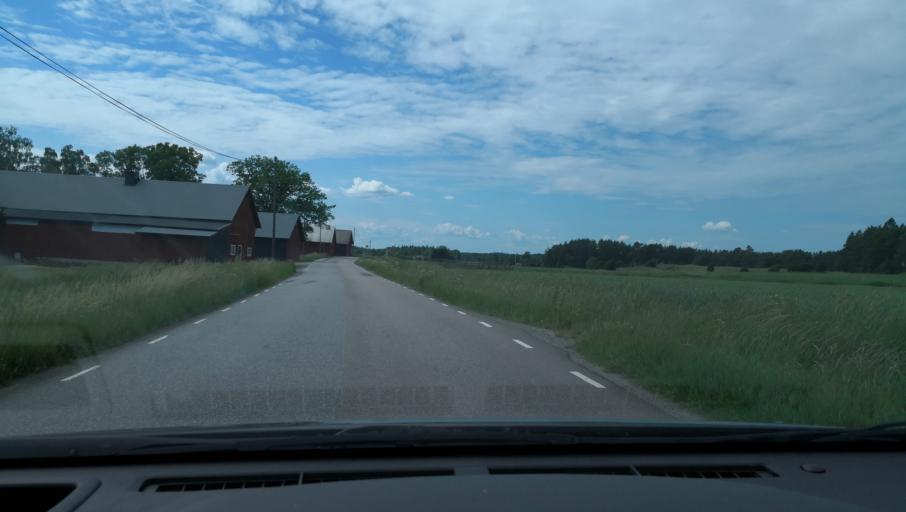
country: SE
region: Uppsala
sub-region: Uppsala Kommun
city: Uppsala
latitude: 59.8123
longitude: 17.5094
